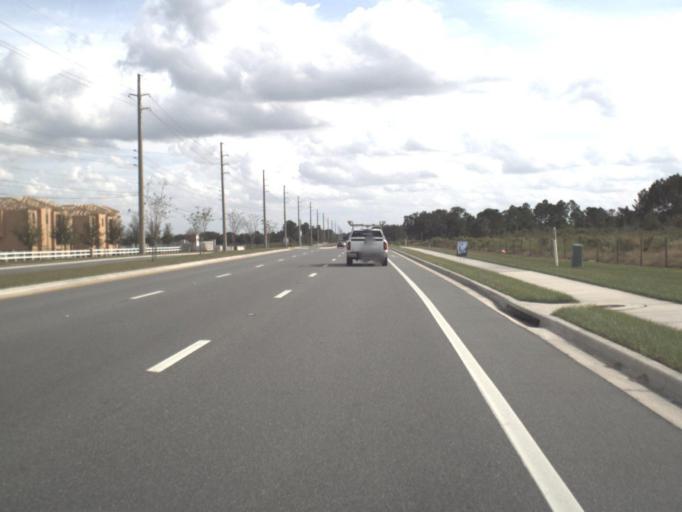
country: US
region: Florida
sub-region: Osceola County
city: Buenaventura Lakes
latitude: 28.3571
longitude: -81.2413
